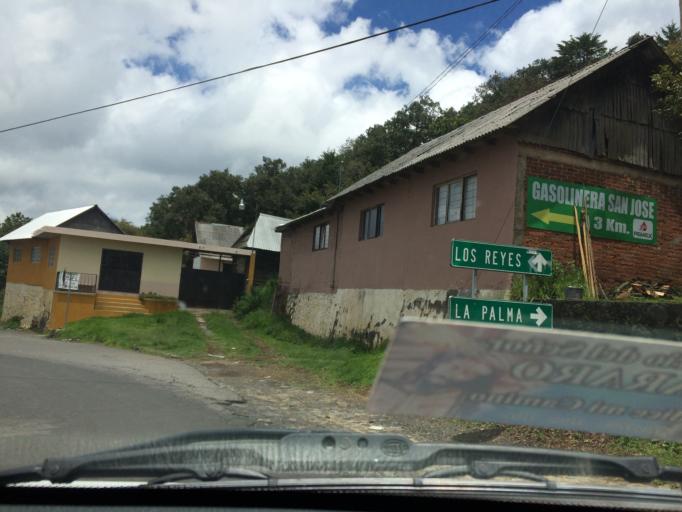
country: MX
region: Michoacan
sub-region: Uruapan
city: Santa Ana Zirosto
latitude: 19.5644
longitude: -102.2907
